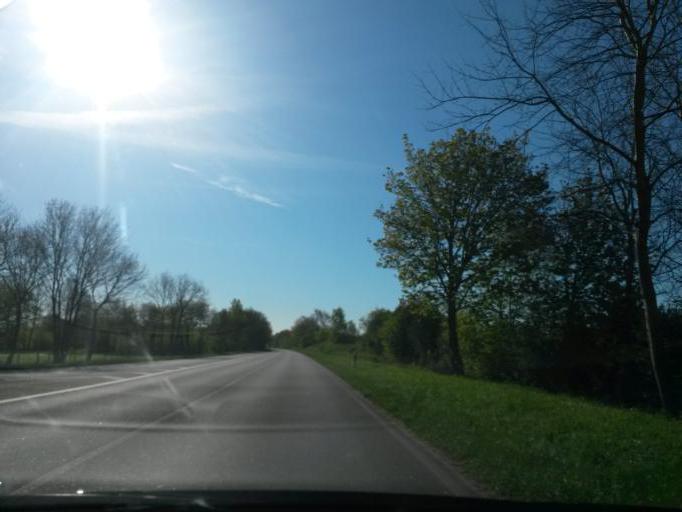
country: DE
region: Schleswig-Holstein
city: Rellingen
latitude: 53.6146
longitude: 9.7945
